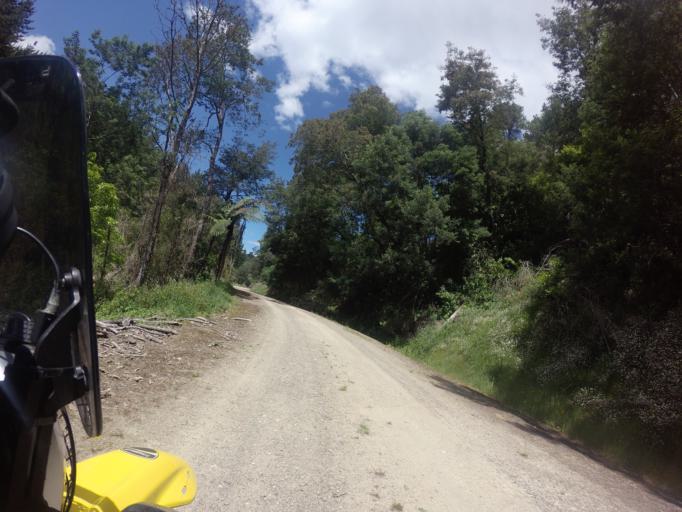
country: NZ
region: Hawke's Bay
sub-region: Wairoa District
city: Wairoa
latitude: -38.9697
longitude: 177.6694
